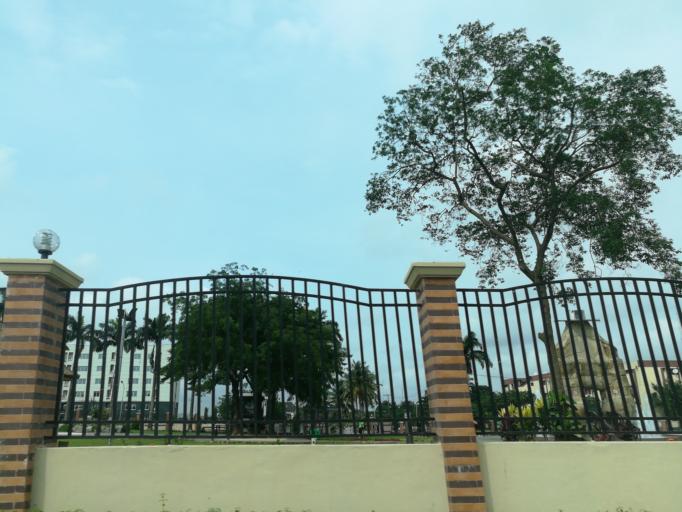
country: NG
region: Lagos
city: Ikeja
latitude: 6.6153
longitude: 3.3642
